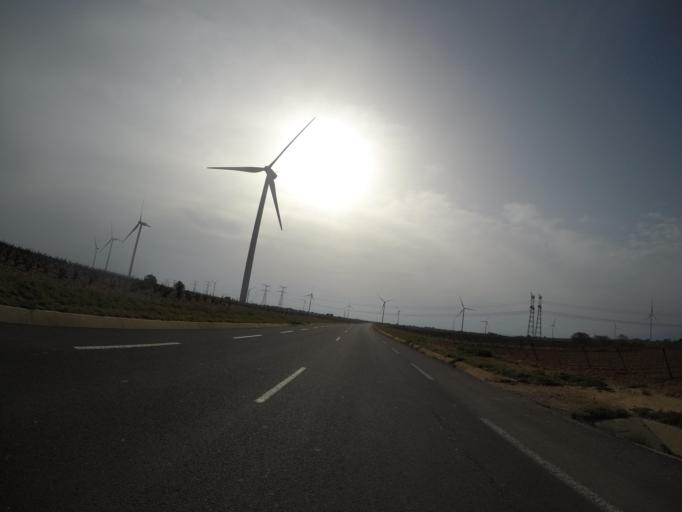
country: FR
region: Languedoc-Roussillon
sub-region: Departement des Pyrenees-Orientales
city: Pezilla-la-Riviere
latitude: 42.7284
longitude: 2.7771
